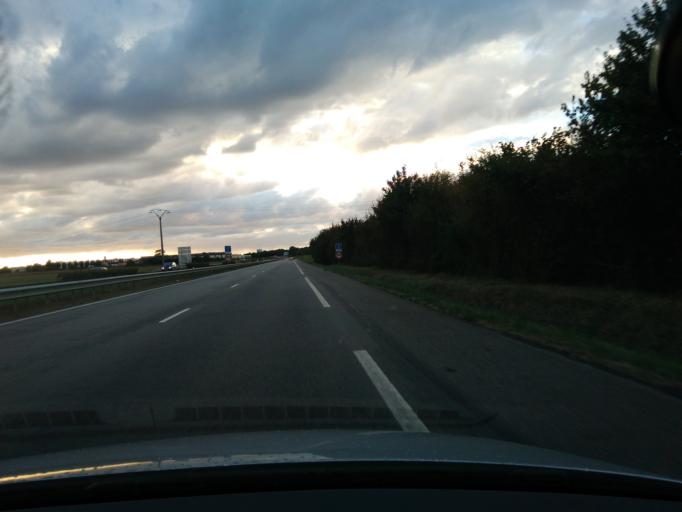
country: FR
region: Haute-Normandie
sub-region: Departement de l'Eure
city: Evreux
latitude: 48.9977
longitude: 1.1674
